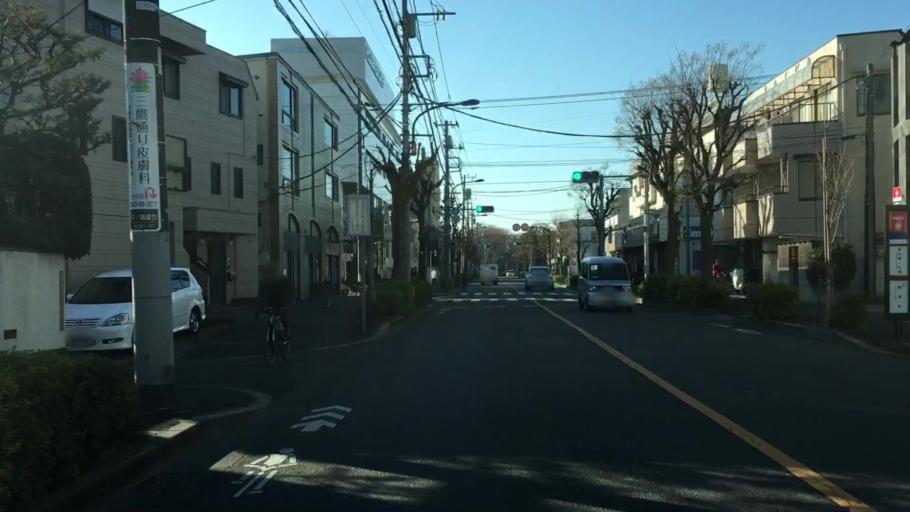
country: JP
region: Tokyo
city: Musashino
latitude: 35.7081
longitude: 139.5567
